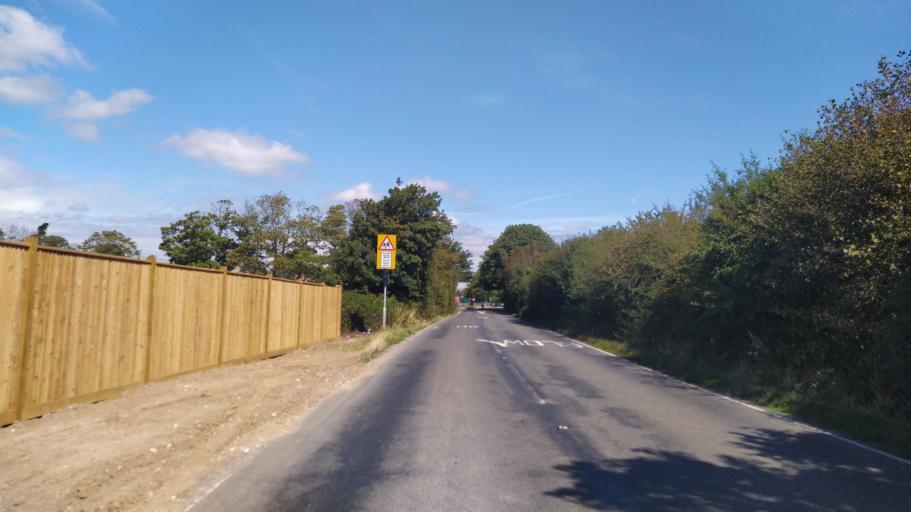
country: GB
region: England
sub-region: West Sussex
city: Chichester
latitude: 50.8204
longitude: -0.7687
